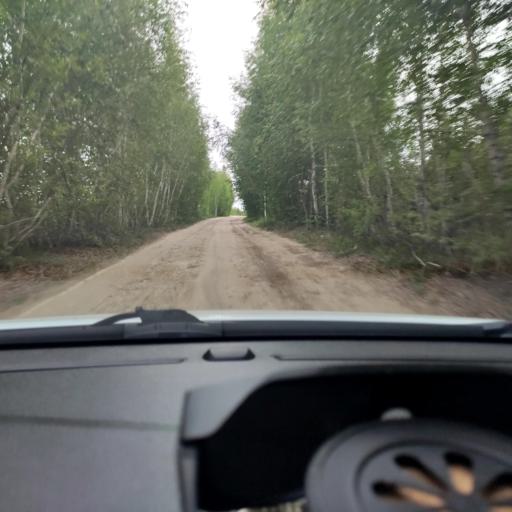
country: RU
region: Tatarstan
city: Vysokaya Gora
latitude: 55.8553
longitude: 49.2503
